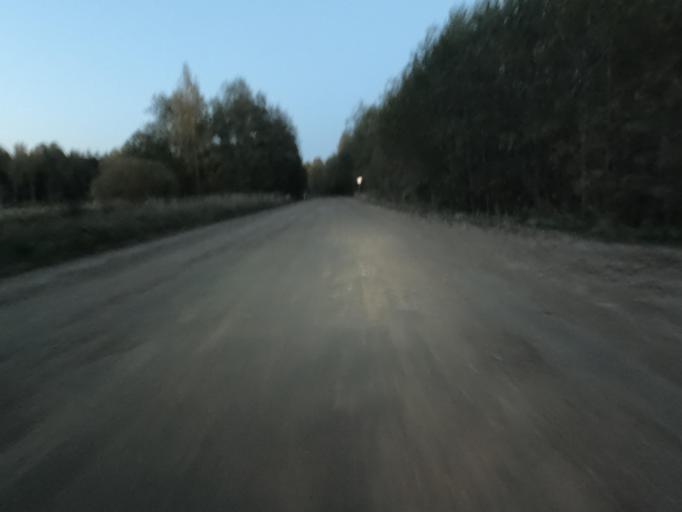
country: RU
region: Leningrad
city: Lyuban'
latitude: 59.1874
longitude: 31.2489
